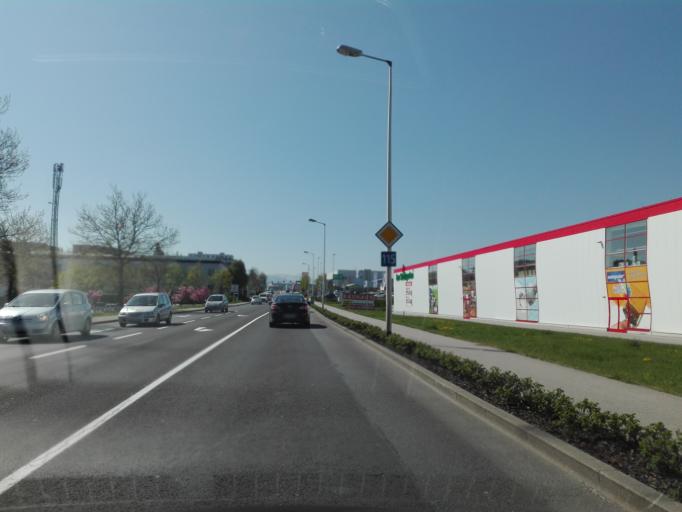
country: AT
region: Upper Austria
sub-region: Steyr Stadt
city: Steyr
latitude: 48.0636
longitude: 14.4210
